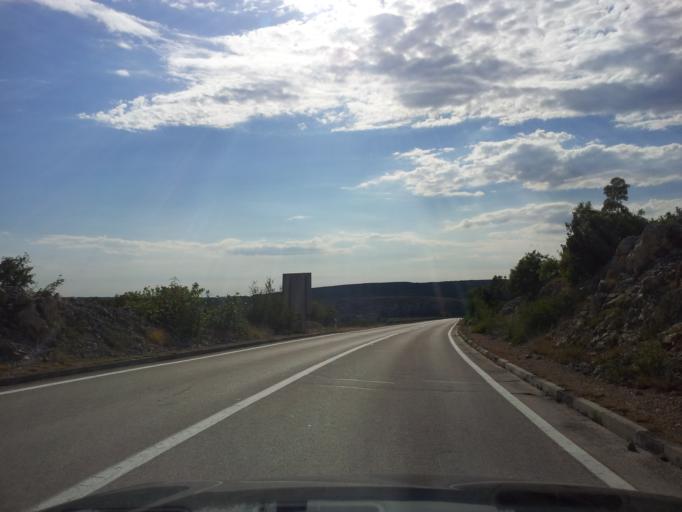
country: HR
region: Zadarska
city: Pridraga
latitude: 44.2281
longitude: 15.5445
